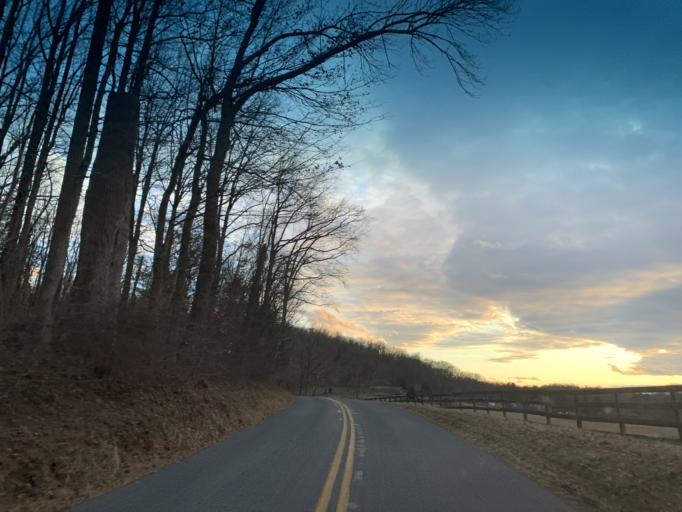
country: US
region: Maryland
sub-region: Harford County
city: Bel Air North
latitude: 39.6082
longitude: -76.3201
